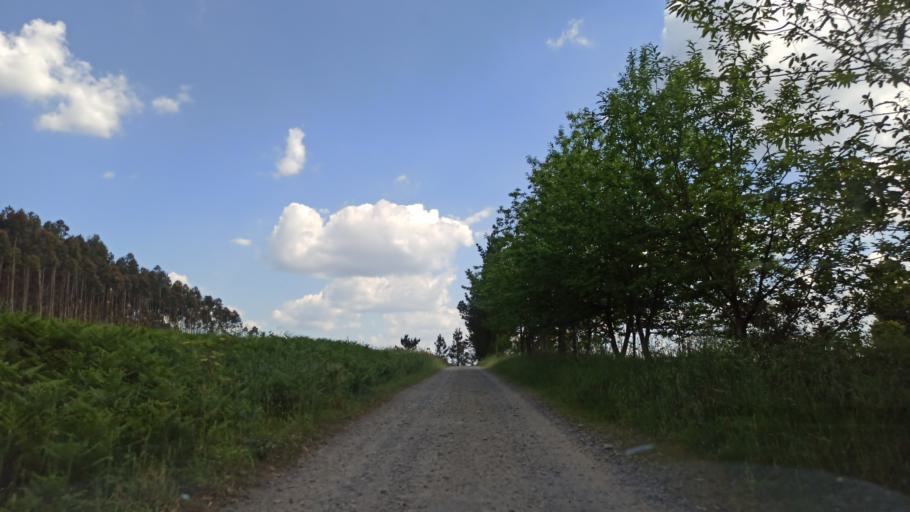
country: ES
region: Galicia
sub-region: Provincia da Coruna
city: Santa Comba
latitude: 43.0755
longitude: -8.7165
